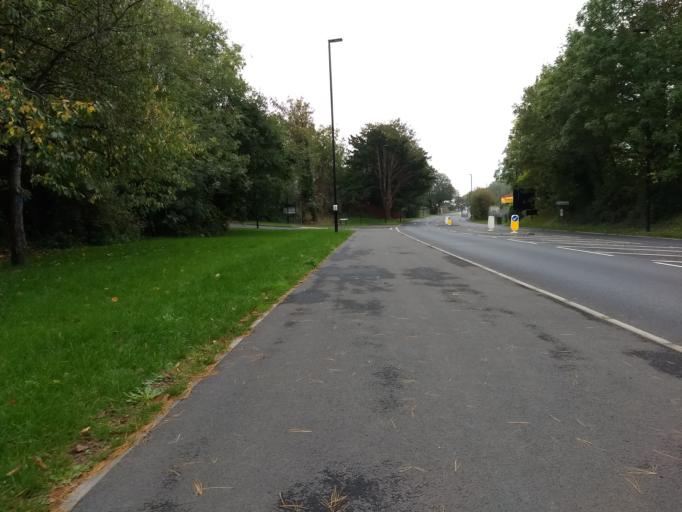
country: GB
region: England
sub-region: Isle of Wight
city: Newport
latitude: 50.6922
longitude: -1.2875
